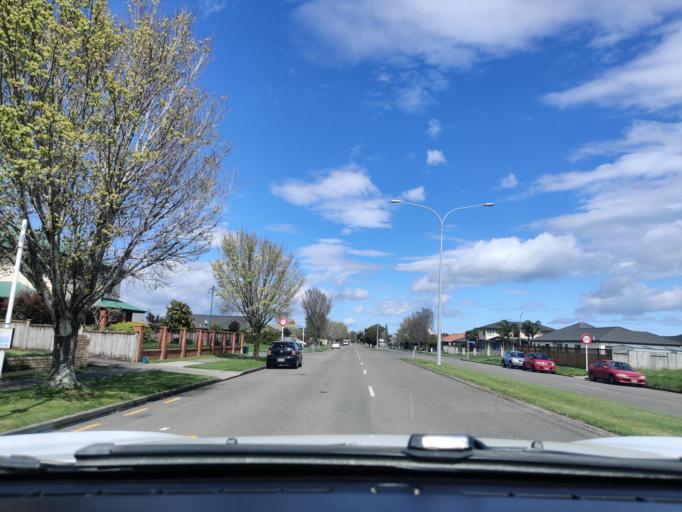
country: NZ
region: Manawatu-Wanganui
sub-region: Palmerston North City
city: Palmerston North
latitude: -40.3243
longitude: 175.6124
